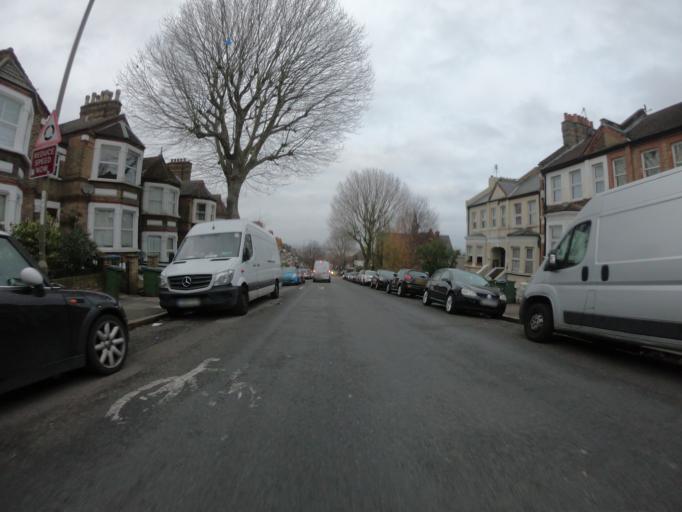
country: GB
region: England
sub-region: Greater London
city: Woolwich
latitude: 51.4848
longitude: 0.0836
